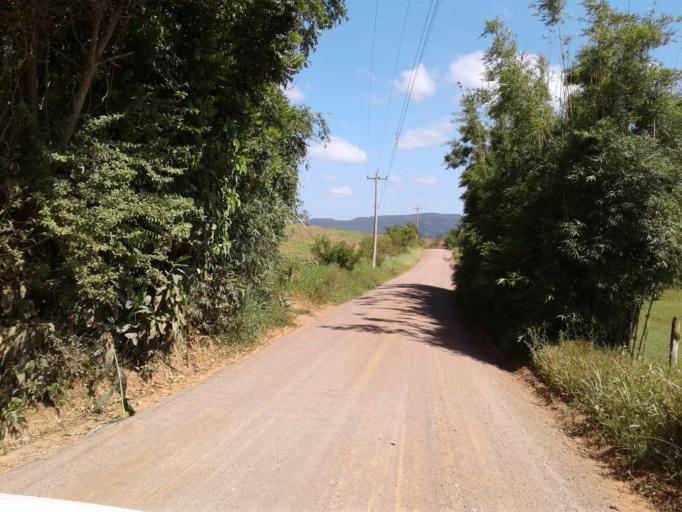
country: BR
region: Rio Grande do Sul
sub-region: Gravatai
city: Gravatai
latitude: -29.8777
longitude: -50.8186
